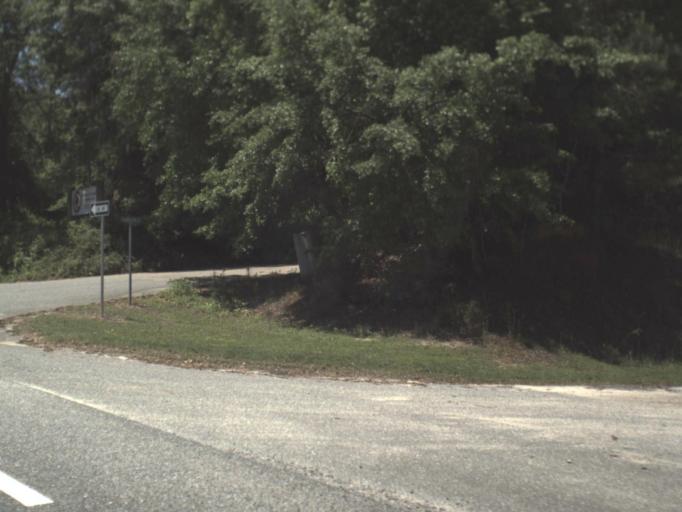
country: US
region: Florida
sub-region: Jefferson County
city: Monticello
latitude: 30.5296
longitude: -83.8714
